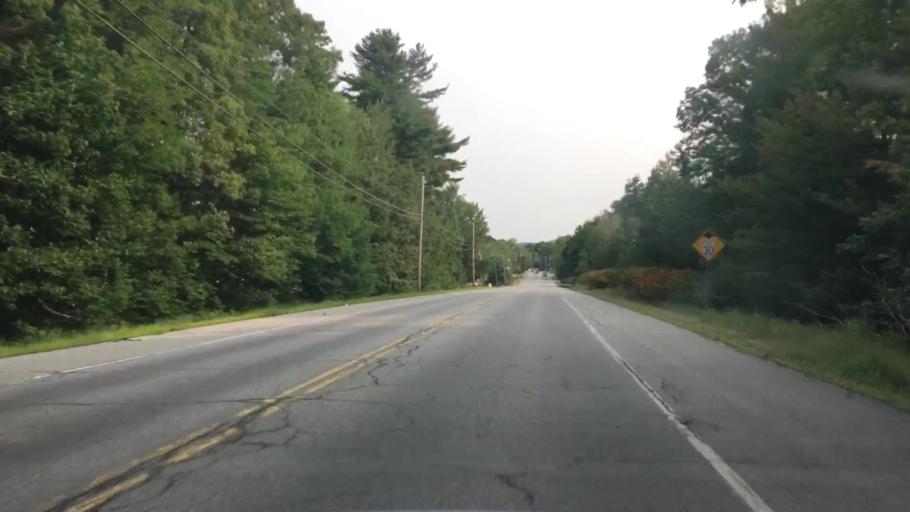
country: US
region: Maine
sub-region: Kennebec County
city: Gardiner
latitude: 44.2136
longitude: -69.7834
